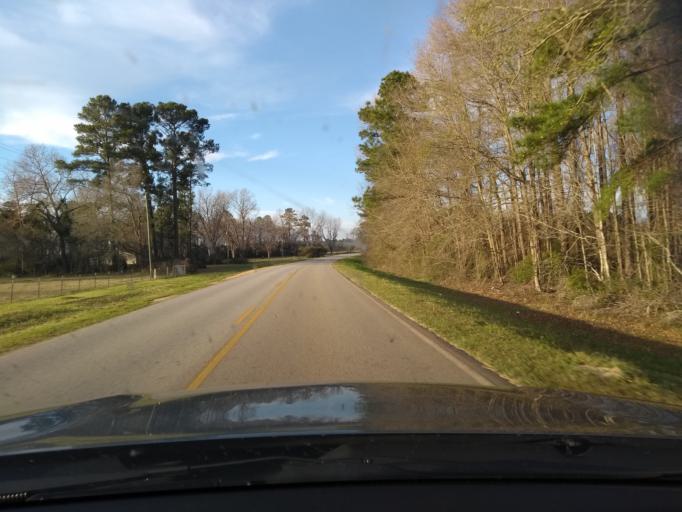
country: US
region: Georgia
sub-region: Bulloch County
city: Statesboro
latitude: 32.3414
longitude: -81.7735
